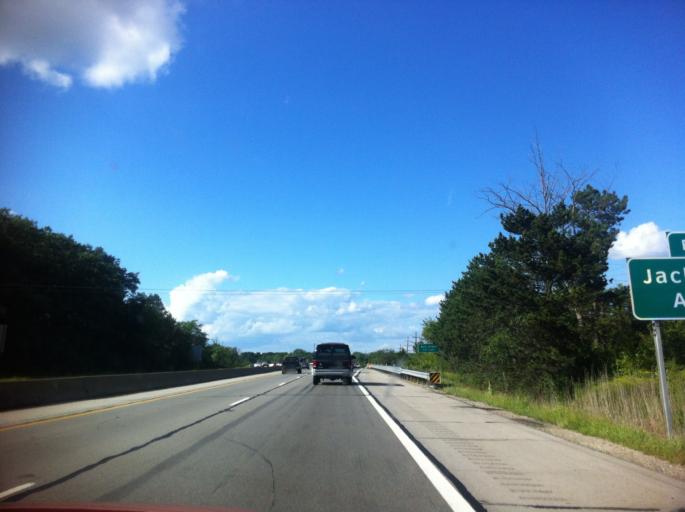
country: US
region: Michigan
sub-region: Washtenaw County
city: Ann Arbor
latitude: 42.2601
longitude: -83.7823
